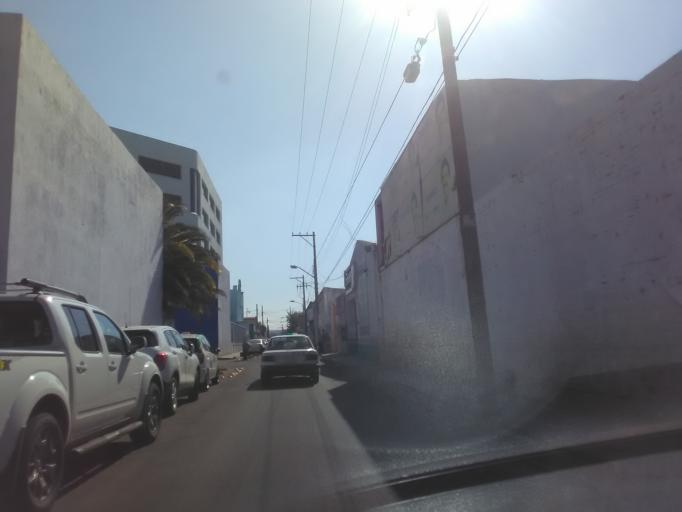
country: MX
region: Durango
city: Victoria de Durango
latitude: 24.0348
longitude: -104.6614
